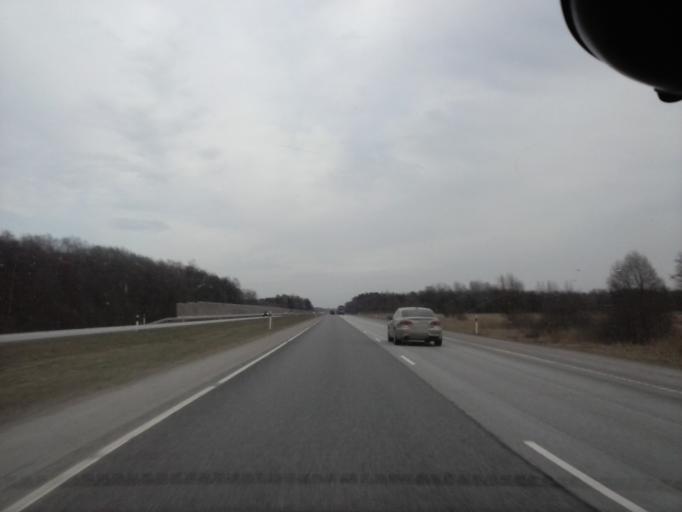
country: EE
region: Harju
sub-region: Rae vald
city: Jueri
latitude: 59.3282
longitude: 24.9167
